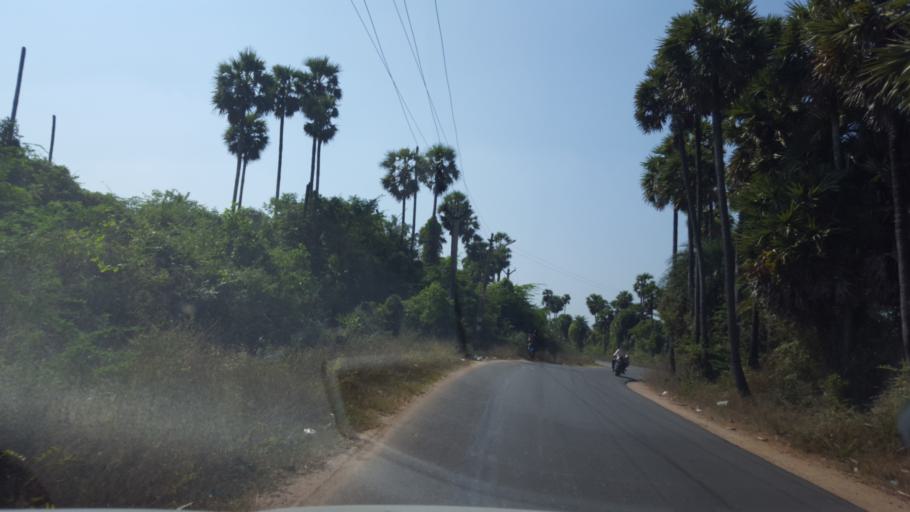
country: IN
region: Tamil Nadu
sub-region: Kancheepuram
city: Kanchipuram
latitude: 12.8380
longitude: 79.7279
